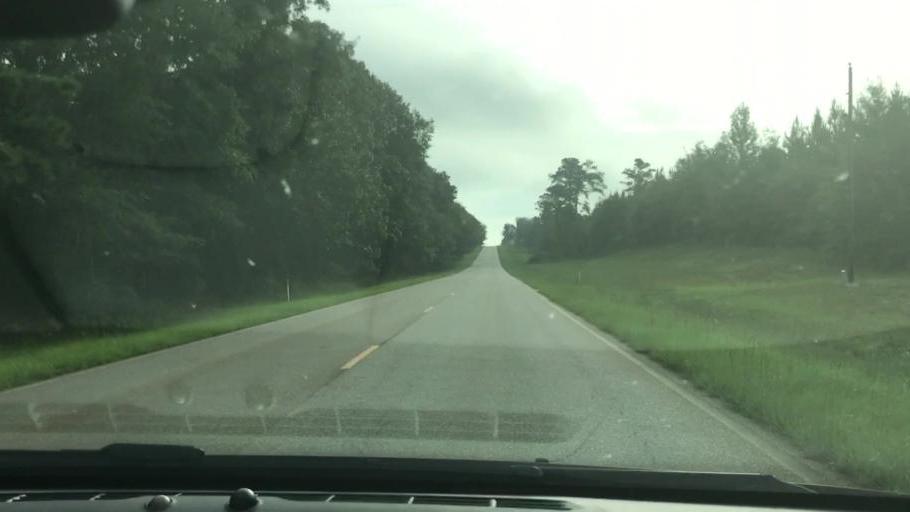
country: US
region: Georgia
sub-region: Stewart County
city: Lumpkin
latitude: 31.9784
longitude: -84.9517
